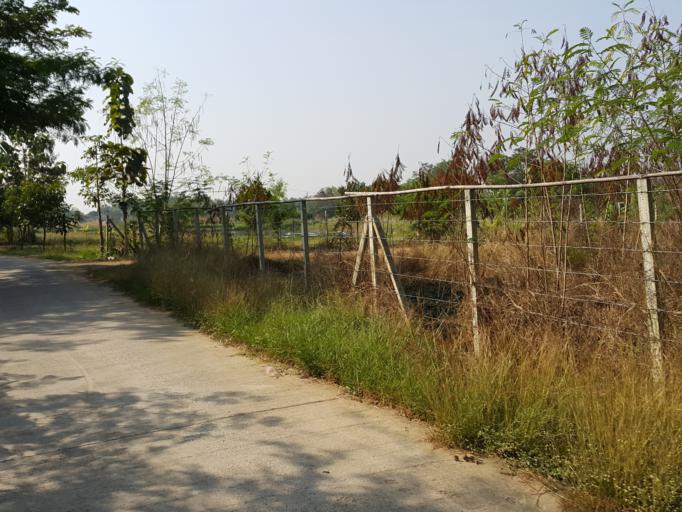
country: TH
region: Chiang Mai
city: San Kamphaeng
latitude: 18.7764
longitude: 99.0961
